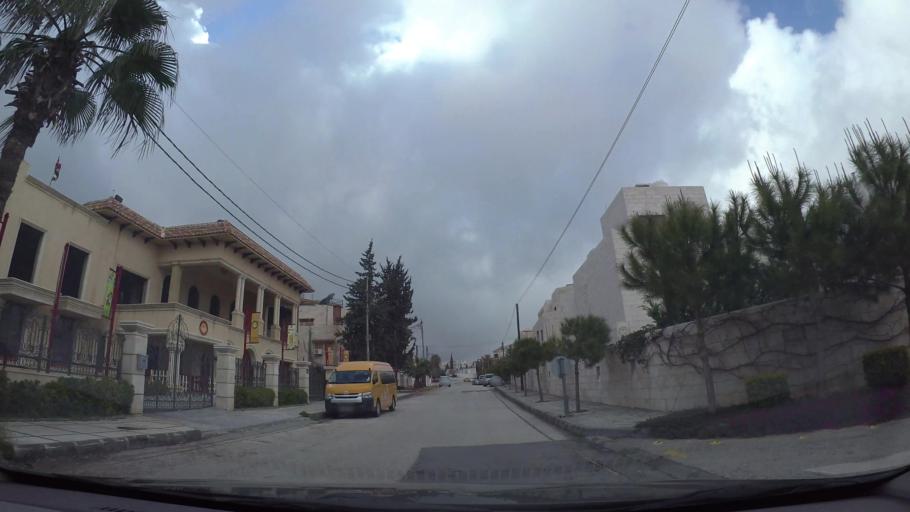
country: JO
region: Amman
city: Amman
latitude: 31.9430
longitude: 35.9025
